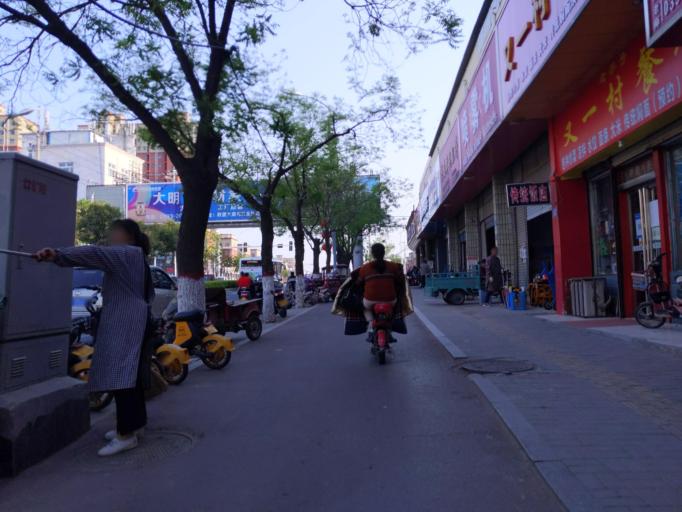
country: CN
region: Henan Sheng
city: Puyang Chengguanzhen
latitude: 35.6992
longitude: 115.0161
